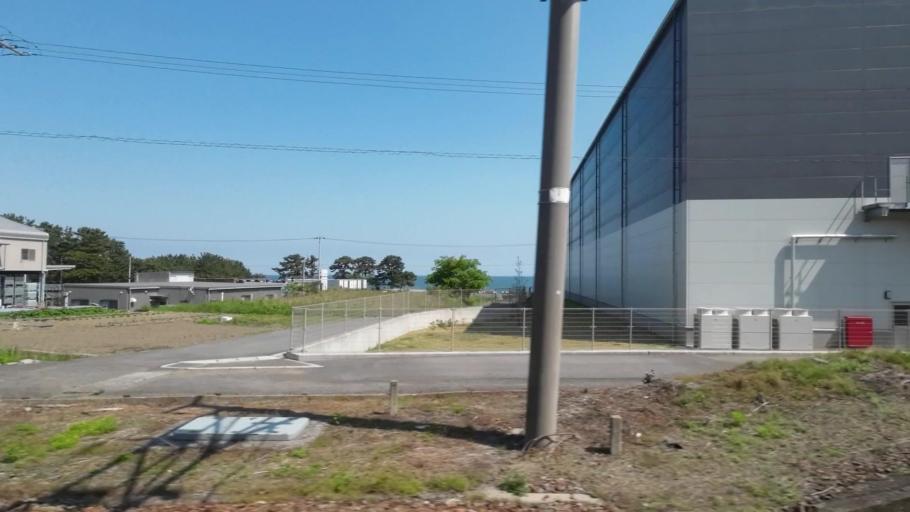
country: JP
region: Ehime
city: Kawanoecho
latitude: 33.9679
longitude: 133.4992
